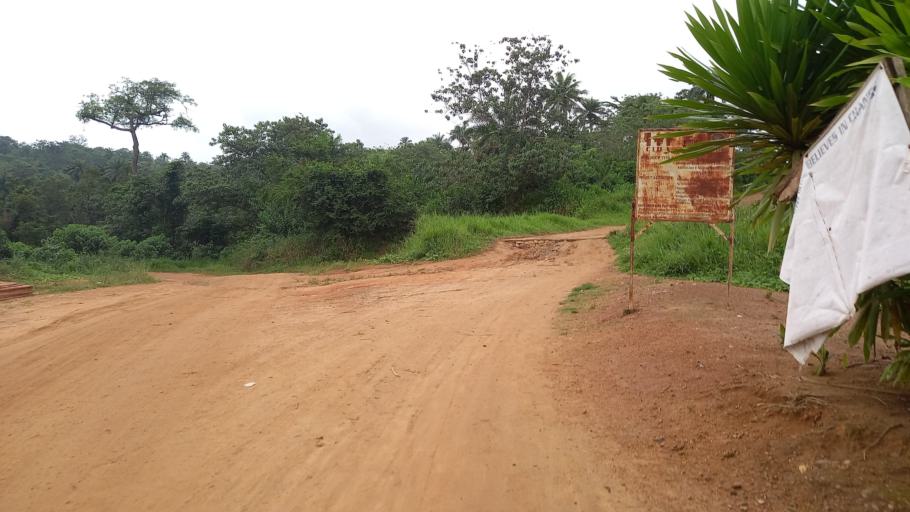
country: SL
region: Eastern Province
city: Kailahun
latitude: 8.2467
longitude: -10.5163
